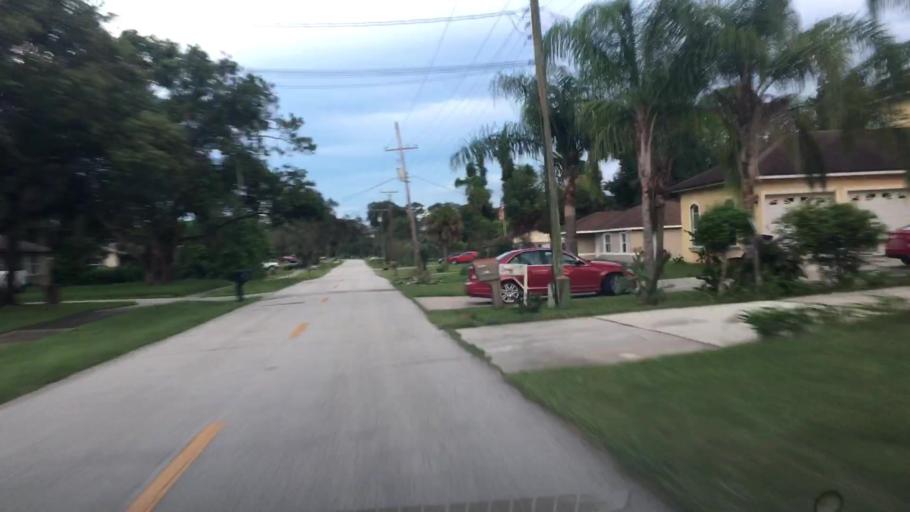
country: US
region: Florida
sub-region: Volusia County
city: DeBary
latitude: 28.8747
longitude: -81.2931
